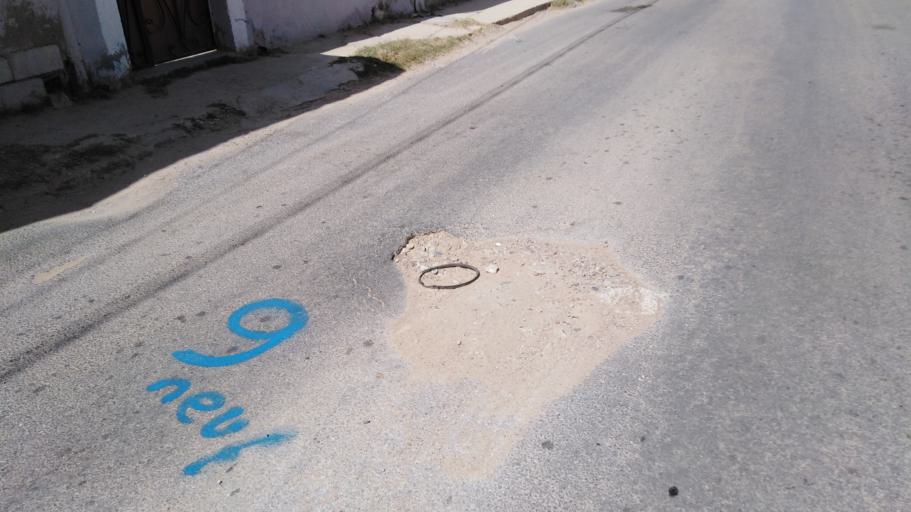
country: TN
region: Qabis
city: Matmata
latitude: 33.6193
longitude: 10.2821
